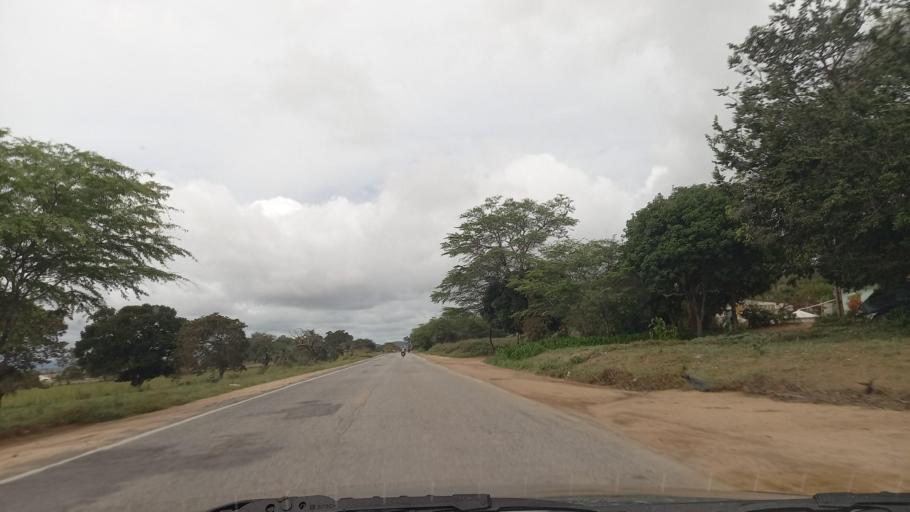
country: BR
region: Pernambuco
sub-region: Sao Joao
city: Sao Joao
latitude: -8.8798
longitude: -36.4241
